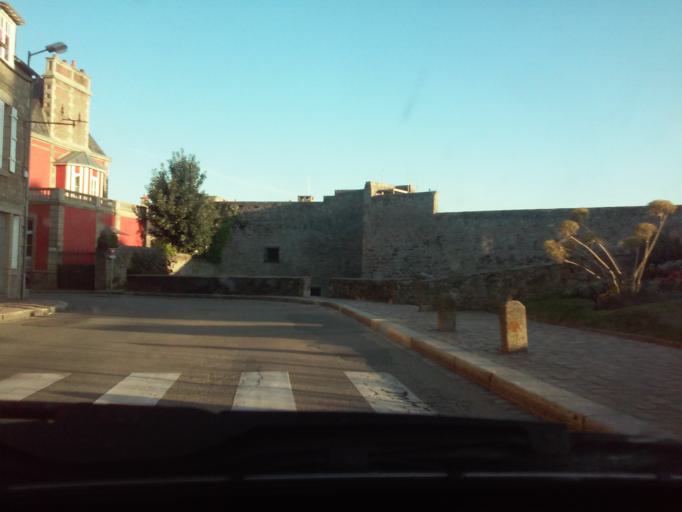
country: FR
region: Brittany
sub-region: Departement des Cotes-d'Armor
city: Lehon
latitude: 48.4504
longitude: -2.0441
